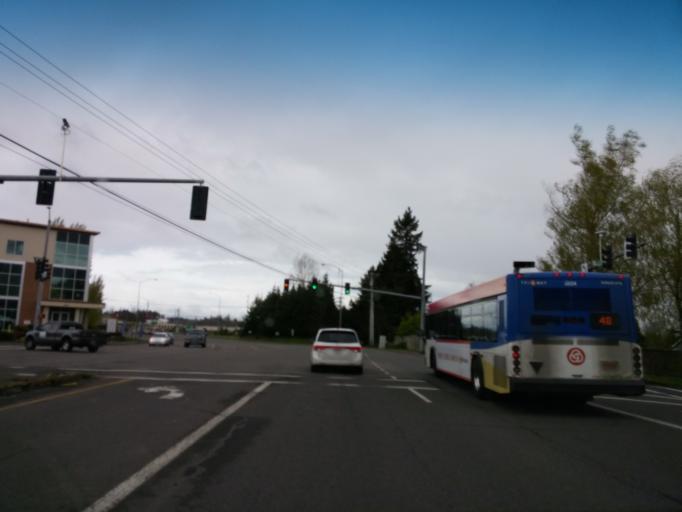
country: US
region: Oregon
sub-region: Washington County
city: Oak Hills
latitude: 45.5319
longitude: -122.8345
